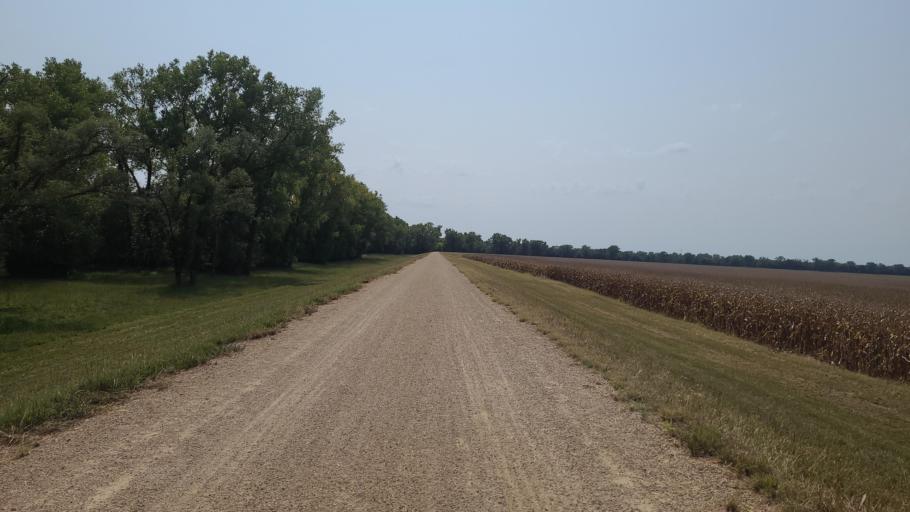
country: US
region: Kansas
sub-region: Douglas County
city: Lawrence
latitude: 38.9775
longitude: -95.1705
